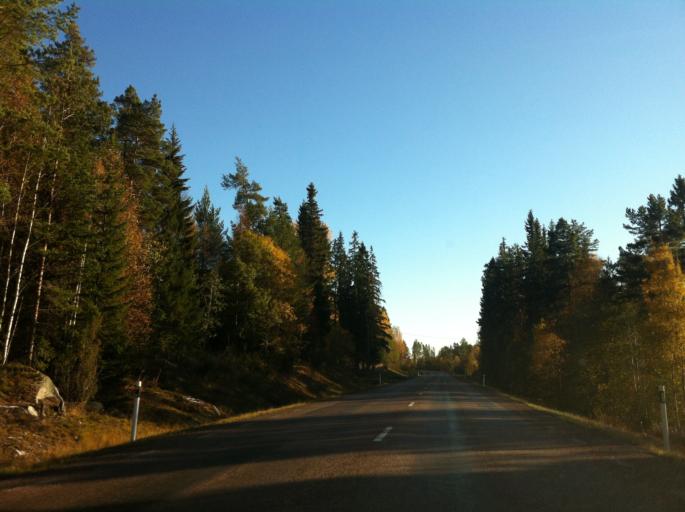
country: SE
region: Dalarna
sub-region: Faluns Kommun
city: Bjursas
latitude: 60.7686
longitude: 15.3180
